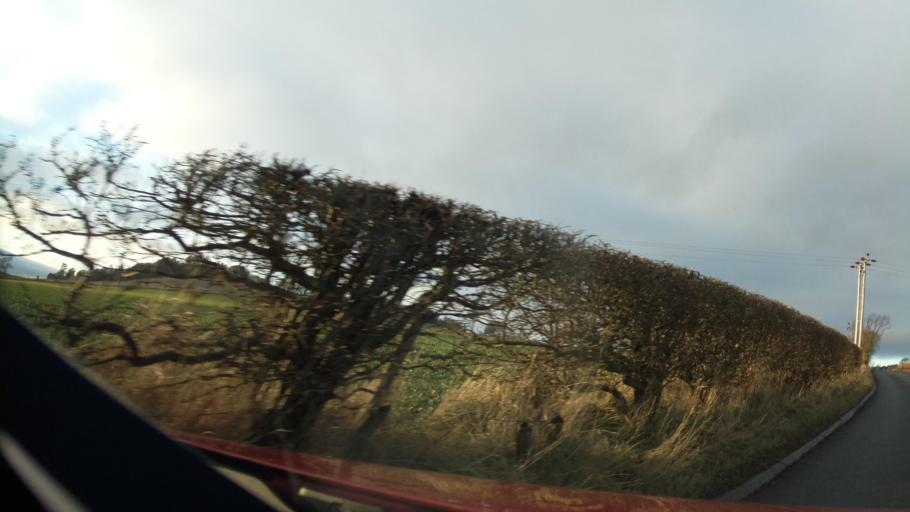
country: GB
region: Scotland
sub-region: Fife
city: Tayport
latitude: 56.5039
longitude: -2.8118
